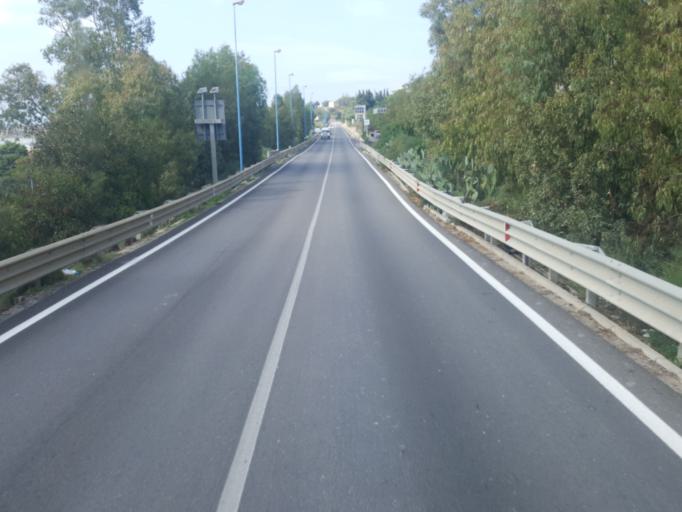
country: IT
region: Sicily
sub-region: Agrigento
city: Porto Empedocle
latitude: 37.2934
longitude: 13.5111
